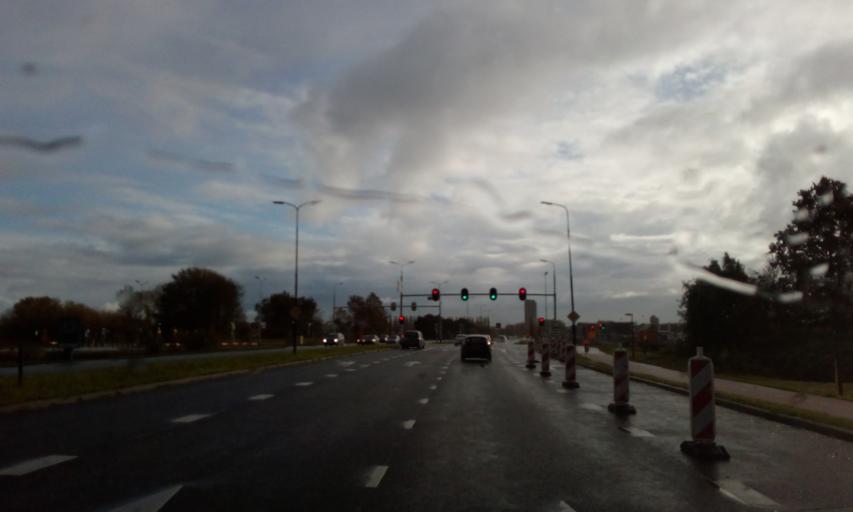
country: NL
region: South Holland
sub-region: Gemeente Rijswijk
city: Rijswijk
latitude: 52.0235
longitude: 4.3265
